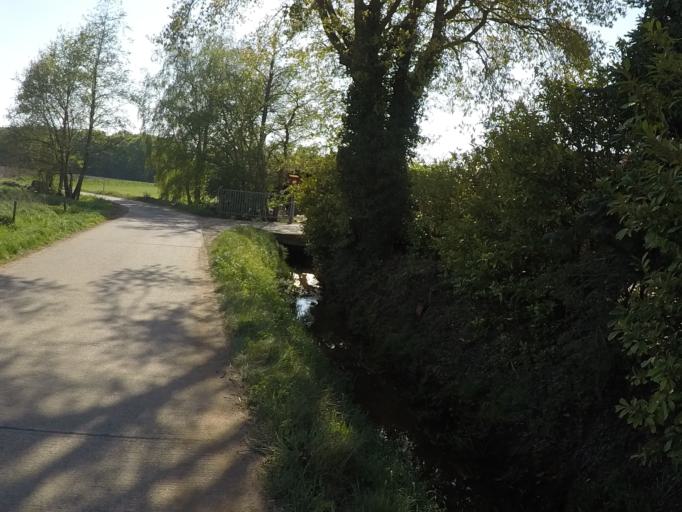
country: BE
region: Flanders
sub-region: Provincie Antwerpen
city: Nijlen
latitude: 51.1588
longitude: 4.6946
